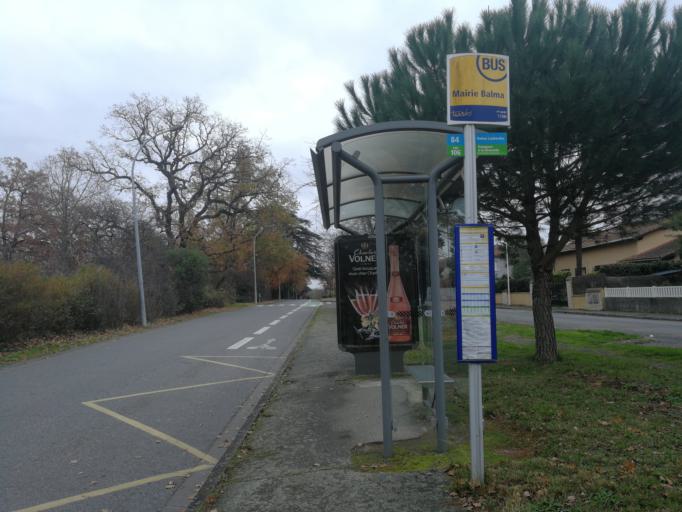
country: FR
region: Midi-Pyrenees
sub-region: Departement de la Haute-Garonne
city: Balma
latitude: 43.6055
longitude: 1.5018
